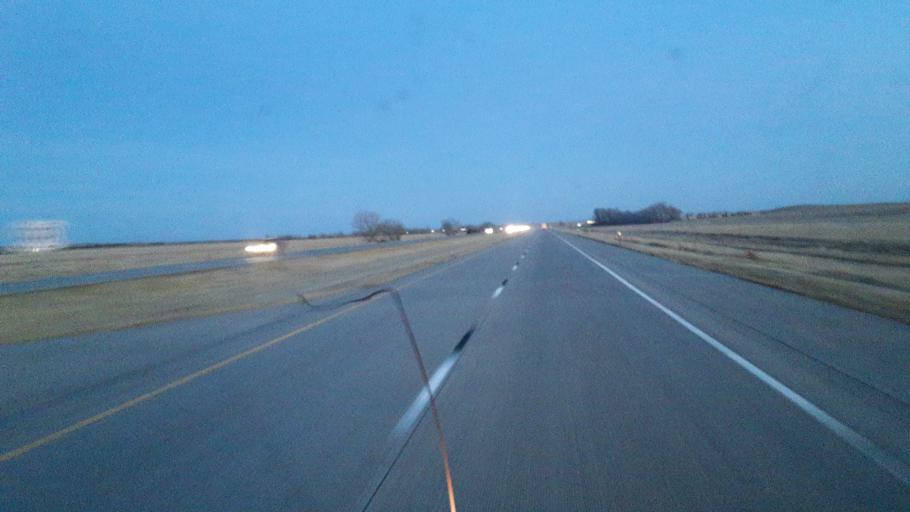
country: US
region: Nebraska
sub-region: Keith County
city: Ogallala
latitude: 41.1084
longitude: -101.5009
